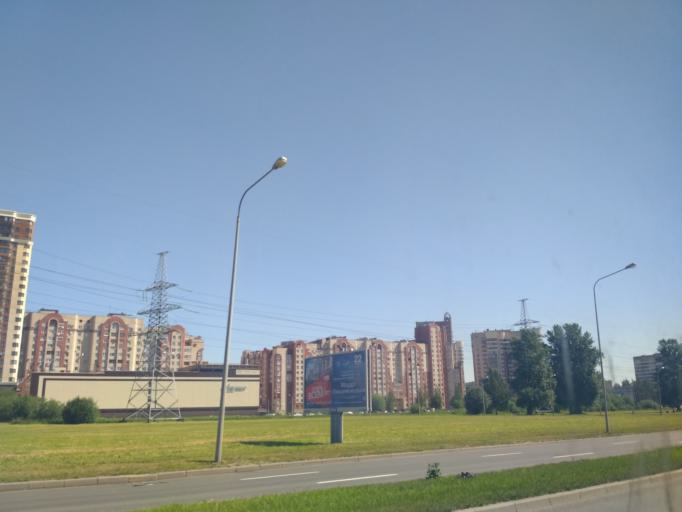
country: RU
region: Leningrad
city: Kalininskiy
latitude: 59.9784
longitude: 30.3860
